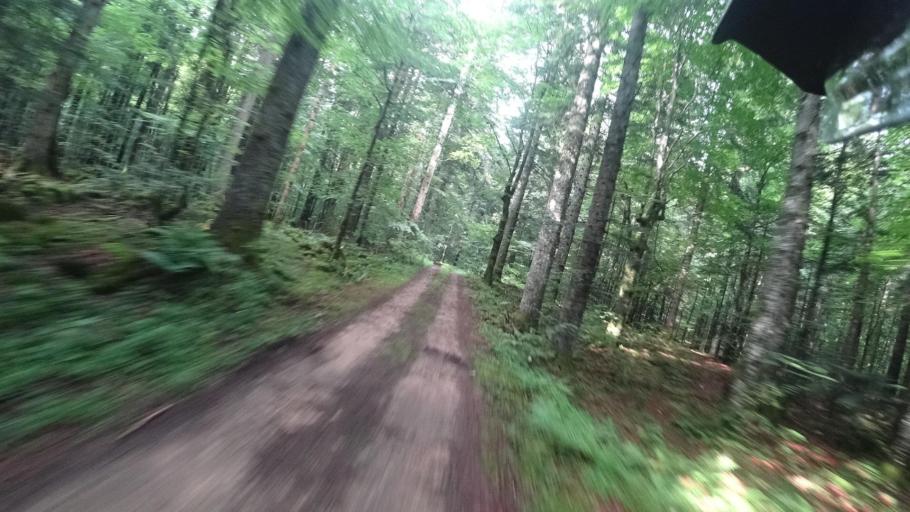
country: HR
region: Licko-Senjska
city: Jezerce
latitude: 44.7963
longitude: 15.6423
